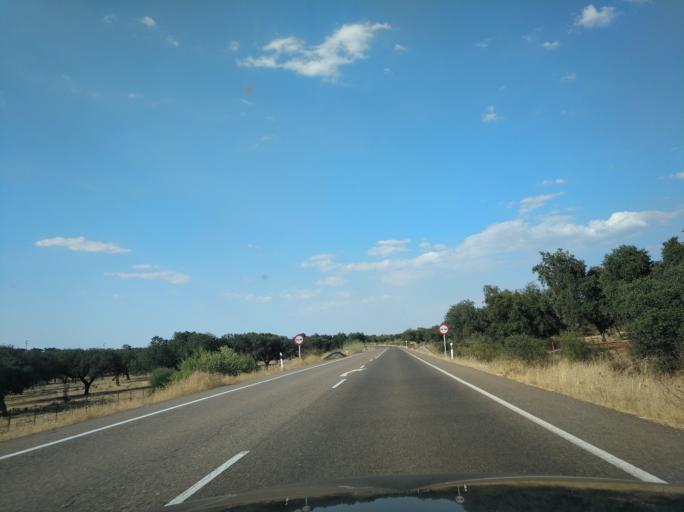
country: ES
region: Extremadura
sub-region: Provincia de Badajoz
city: Villanueva del Fresno
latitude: 38.3947
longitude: -7.1459
